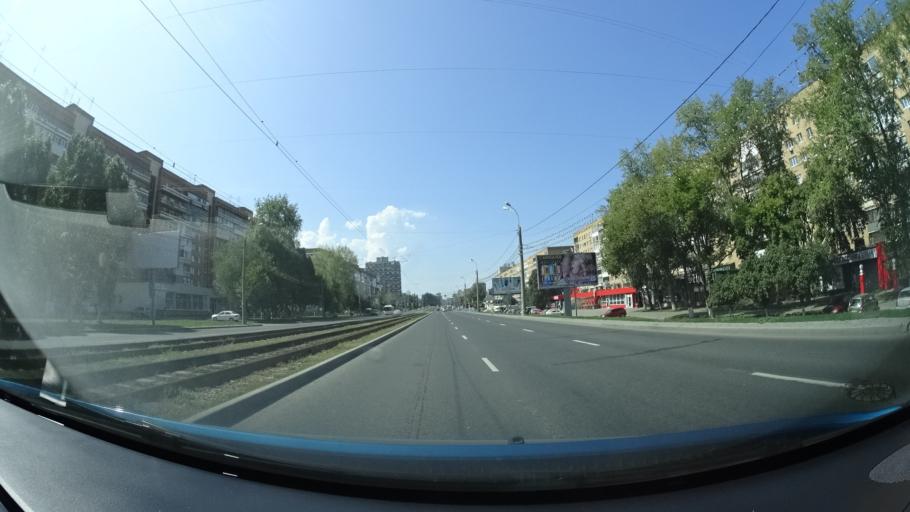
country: RU
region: Samara
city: Samara
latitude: 53.2115
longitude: 50.1428
